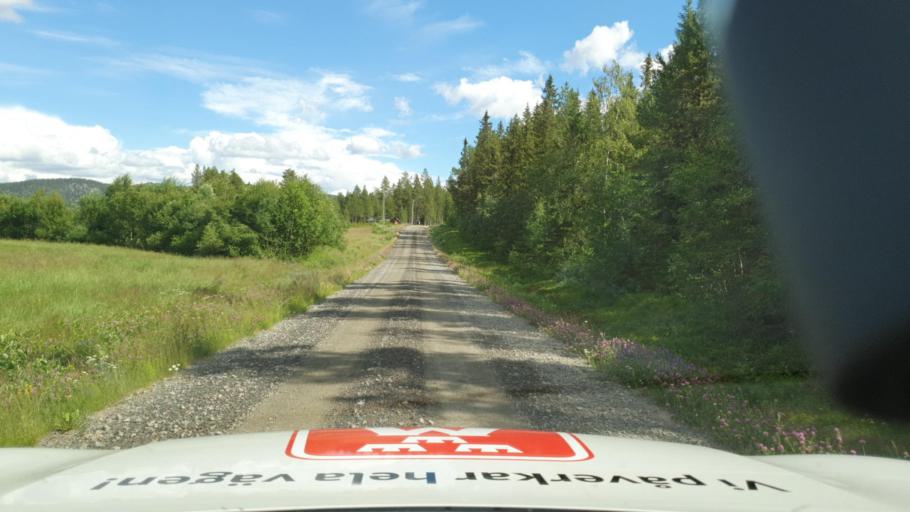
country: SE
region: Vaesterbotten
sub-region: Sorsele Kommun
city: Sorsele
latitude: 65.6431
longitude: 17.4008
